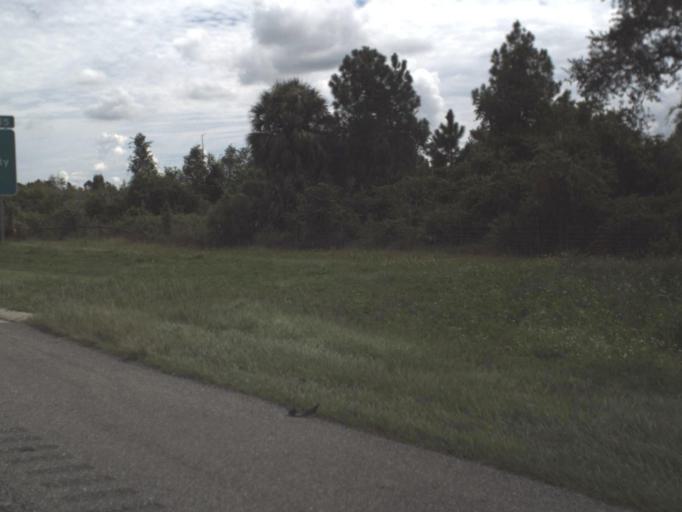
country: US
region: Florida
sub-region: Polk County
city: Davenport
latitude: 28.2180
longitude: -81.6686
